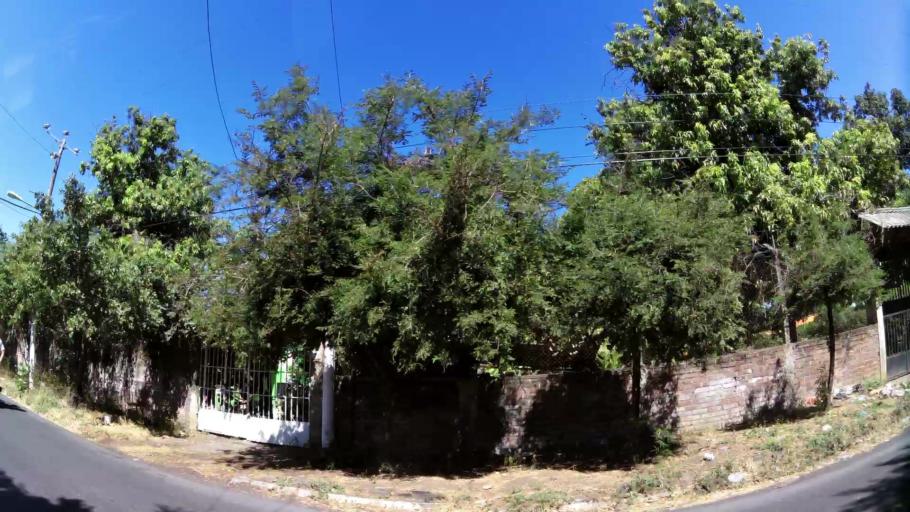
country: SV
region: San Miguel
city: San Miguel
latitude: 13.4821
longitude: -88.1706
